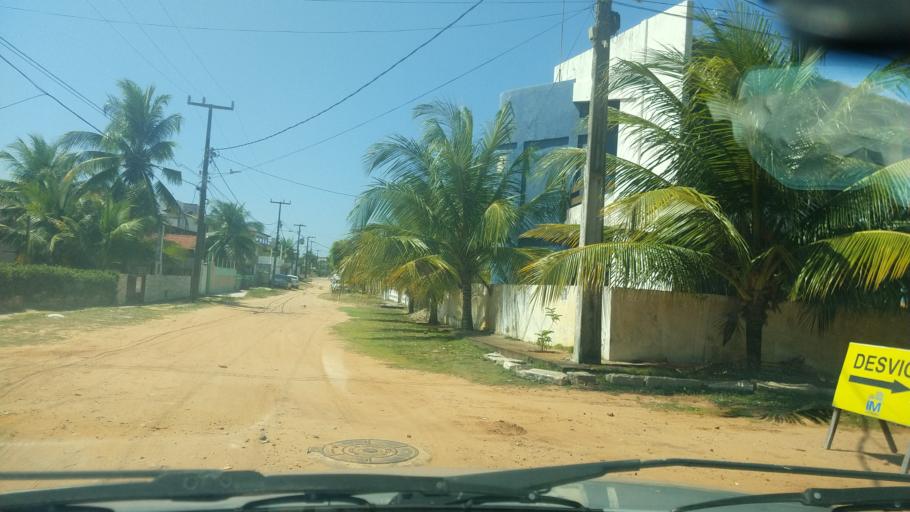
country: BR
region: Rio Grande do Norte
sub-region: Parnamirim
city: Parnamirim
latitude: -5.9557
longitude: -35.1518
